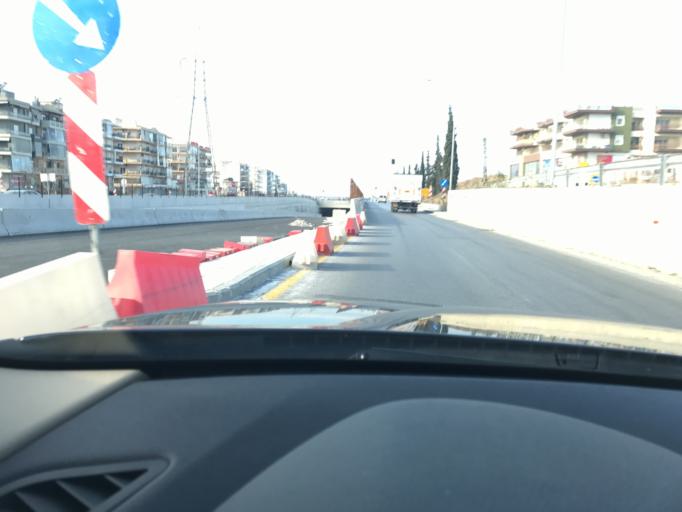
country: GR
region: Central Macedonia
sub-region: Nomos Thessalonikis
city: Evosmos
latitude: 40.6779
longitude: 22.9094
